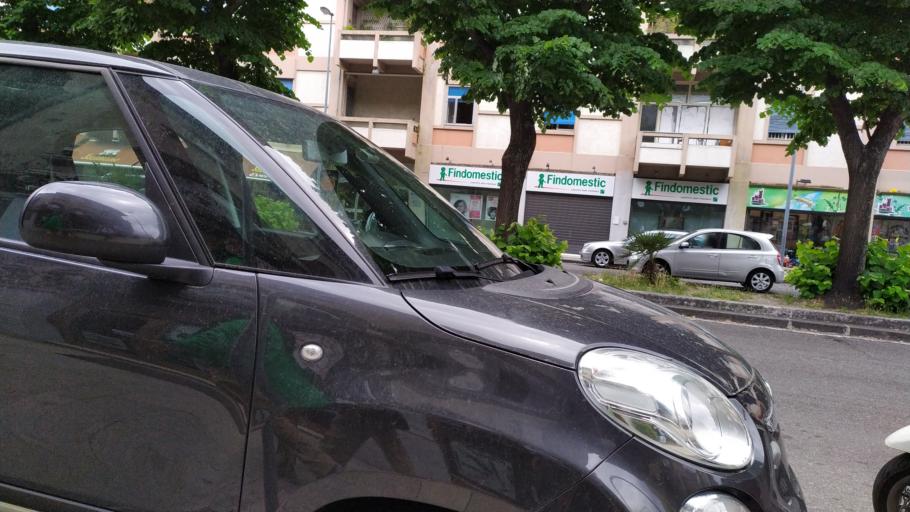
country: IT
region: Sicily
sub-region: Messina
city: Messina
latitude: 38.1915
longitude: 15.5565
